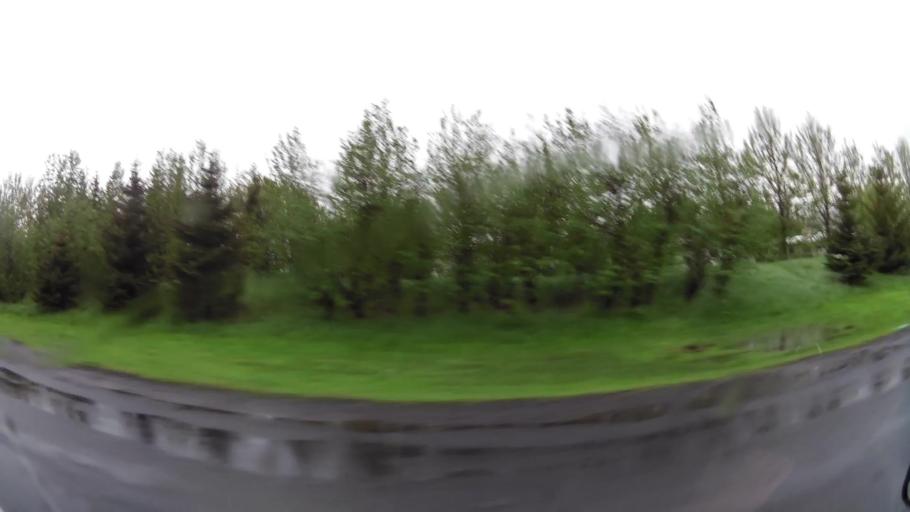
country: IS
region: South
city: Selfoss
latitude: 63.9367
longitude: -20.9790
